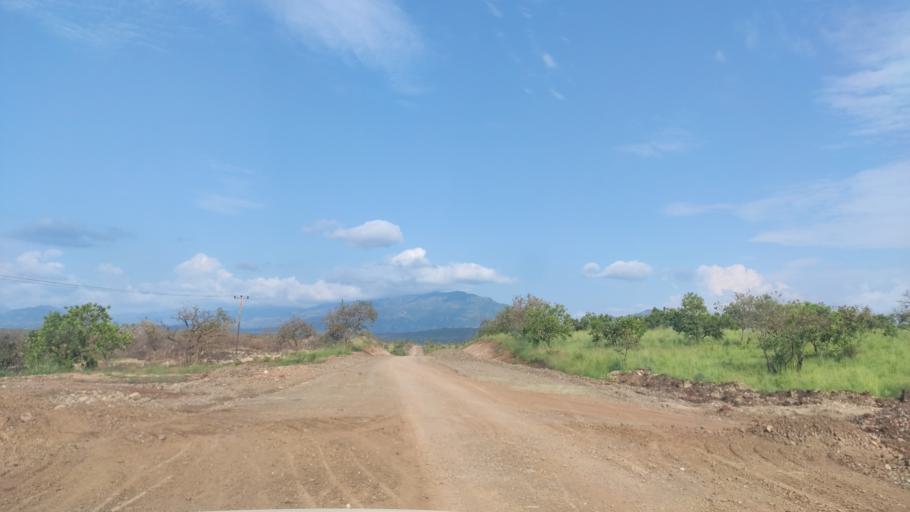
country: ET
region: Southern Nations, Nationalities, and People's Region
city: Felege Neway
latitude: 6.4253
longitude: 37.2488
